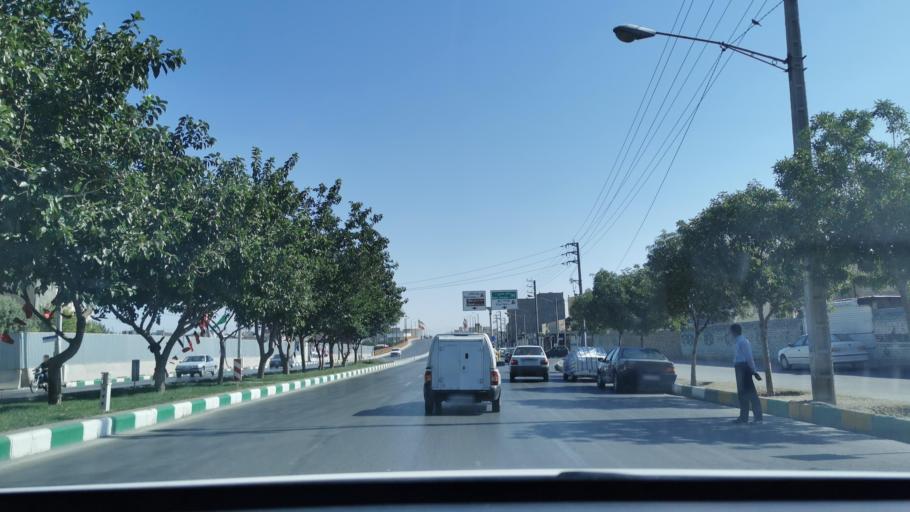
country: IR
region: Razavi Khorasan
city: Mashhad
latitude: 36.3340
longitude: 59.6031
